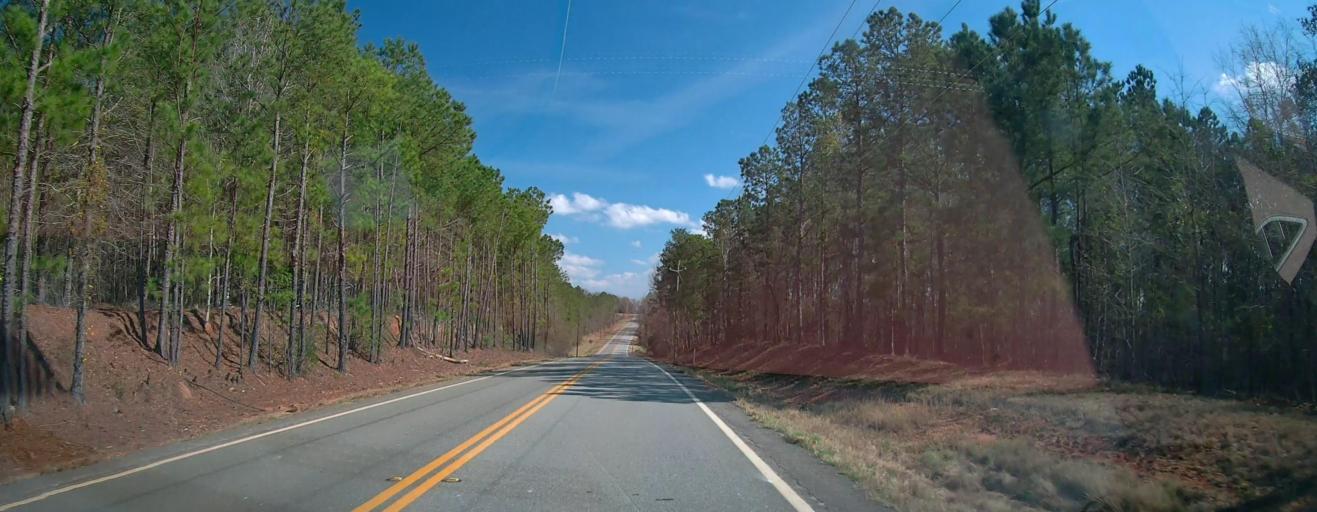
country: US
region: Georgia
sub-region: Wilkinson County
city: Gordon
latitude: 32.8449
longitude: -83.3380
